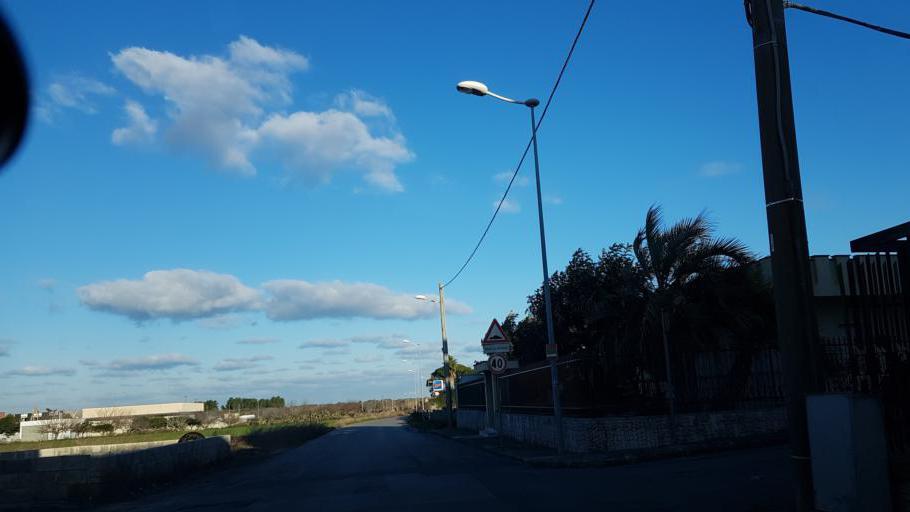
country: IT
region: Apulia
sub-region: Provincia di Lecce
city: Squinzano
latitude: 40.4344
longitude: 18.0533
